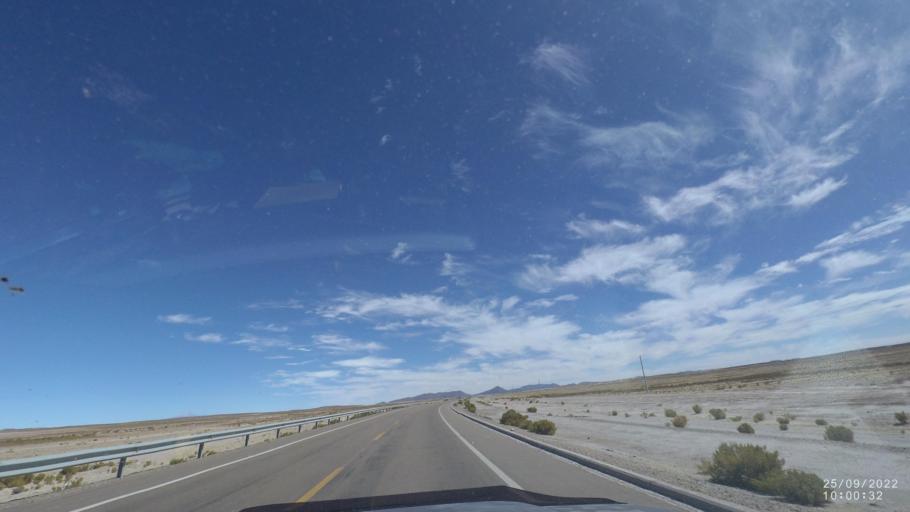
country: BO
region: Potosi
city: Colchani
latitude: -20.2722
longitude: -66.9483
